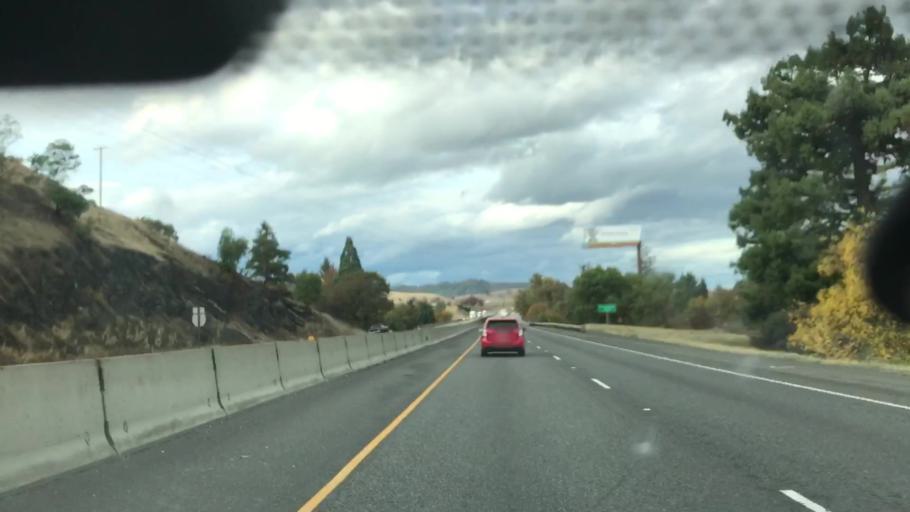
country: US
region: Oregon
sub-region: Douglas County
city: Roseburg North
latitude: 43.2785
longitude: -123.3553
